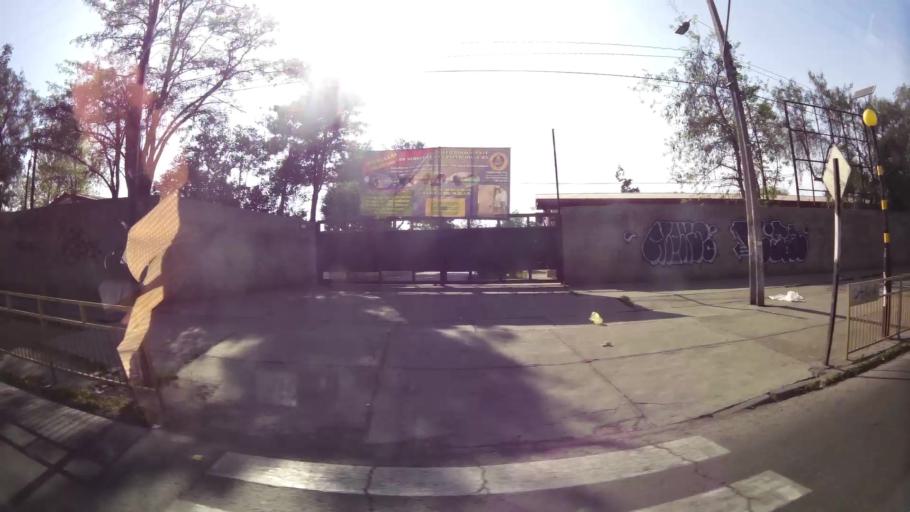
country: CL
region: Santiago Metropolitan
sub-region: Provincia de Santiago
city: Lo Prado
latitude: -33.4193
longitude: -70.7526
